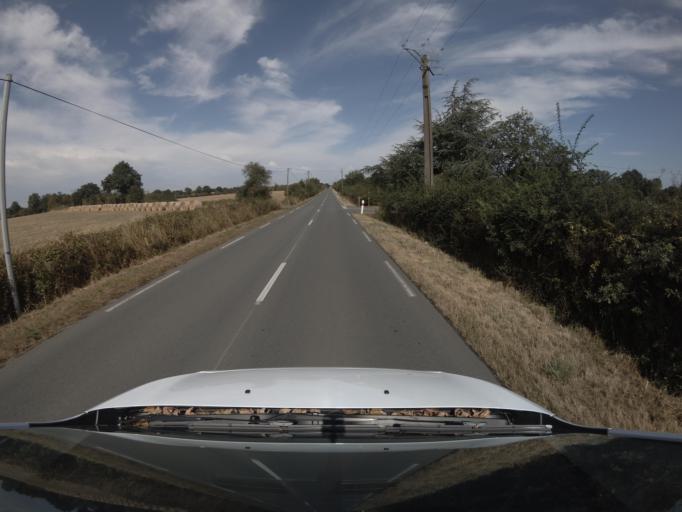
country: FR
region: Poitou-Charentes
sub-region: Departement des Deux-Sevres
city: Nueil-les-Aubiers
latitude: 46.9626
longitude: -0.5732
